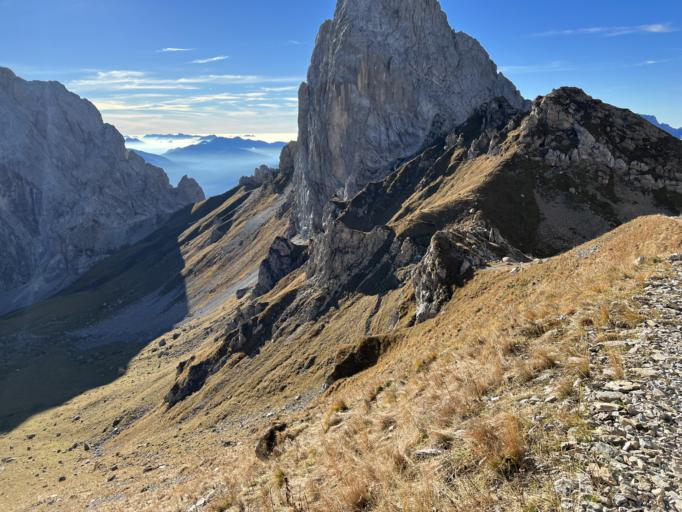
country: IT
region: Friuli Venezia Giulia
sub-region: Provincia di Udine
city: Forni Avoltri
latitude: 46.6298
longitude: 12.7273
